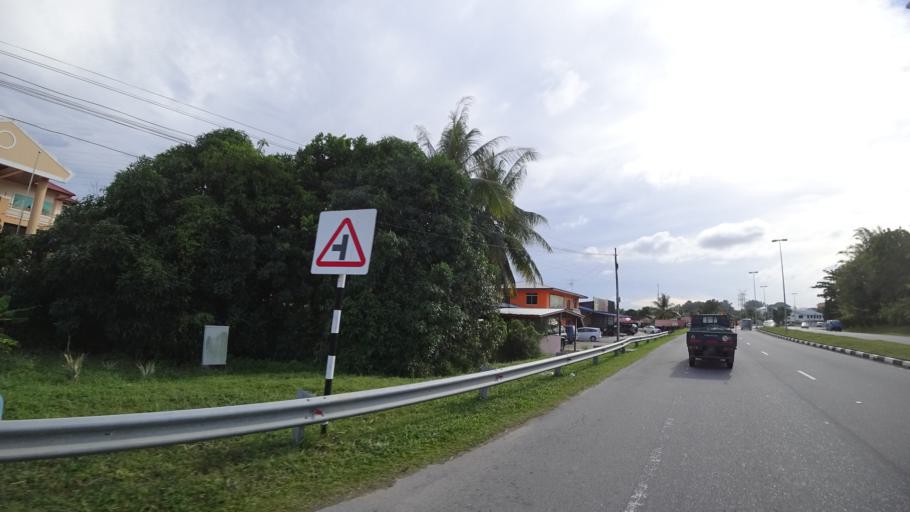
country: BN
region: Brunei and Muara
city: Bandar Seri Begawan
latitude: 4.8792
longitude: 114.8698
